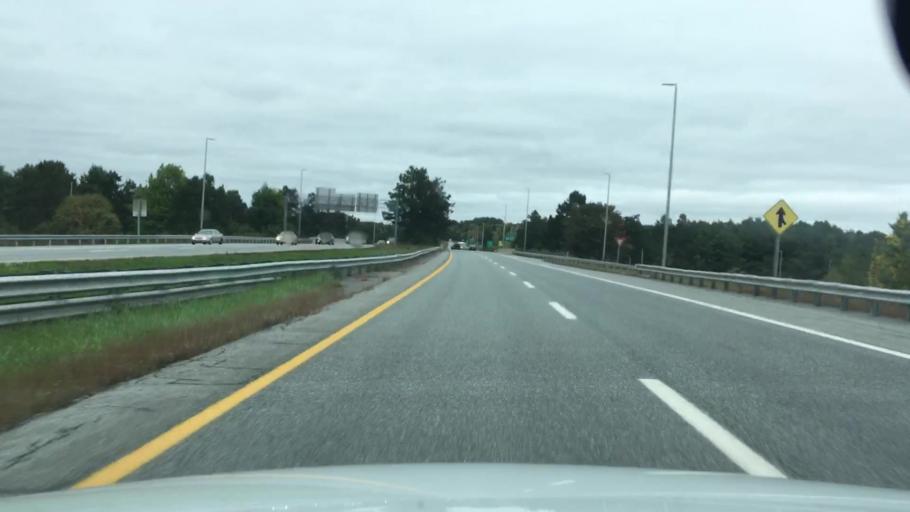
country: US
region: Maine
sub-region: Penobscot County
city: Bangor
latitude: 44.7856
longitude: -68.8092
